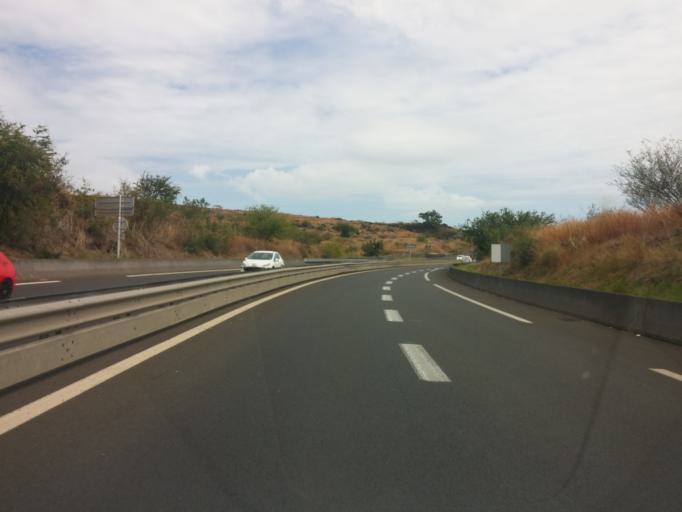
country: RE
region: Reunion
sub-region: Reunion
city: Saint-Paul
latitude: -21.0199
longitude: 55.2621
